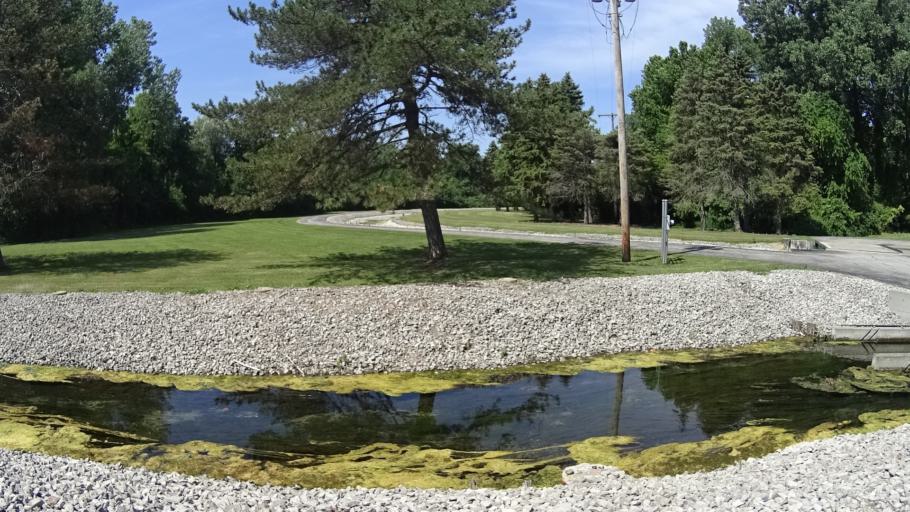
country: US
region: Ohio
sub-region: Erie County
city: Sandusky
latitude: 41.4146
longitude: -82.8066
